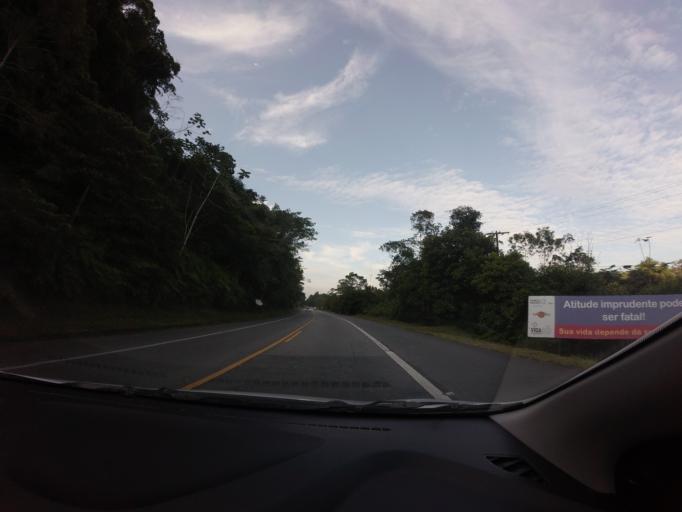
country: BR
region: Sao Paulo
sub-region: Bertioga
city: Bertioga
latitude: -23.8687
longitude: -46.1716
